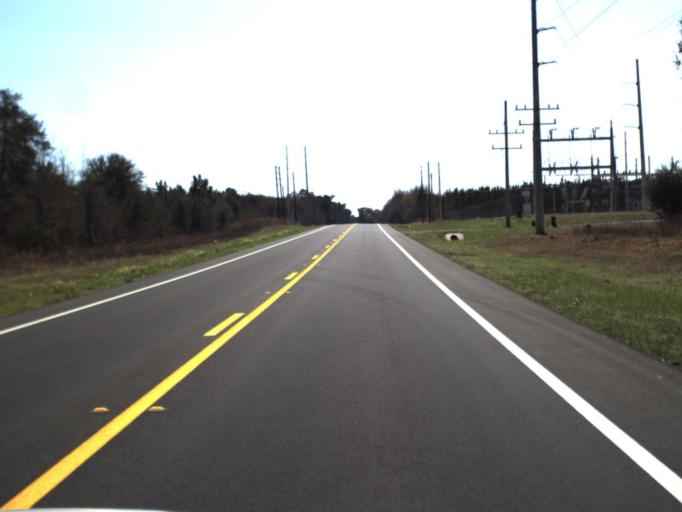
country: US
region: Florida
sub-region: Jackson County
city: Sneads
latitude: 30.7415
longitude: -85.0197
